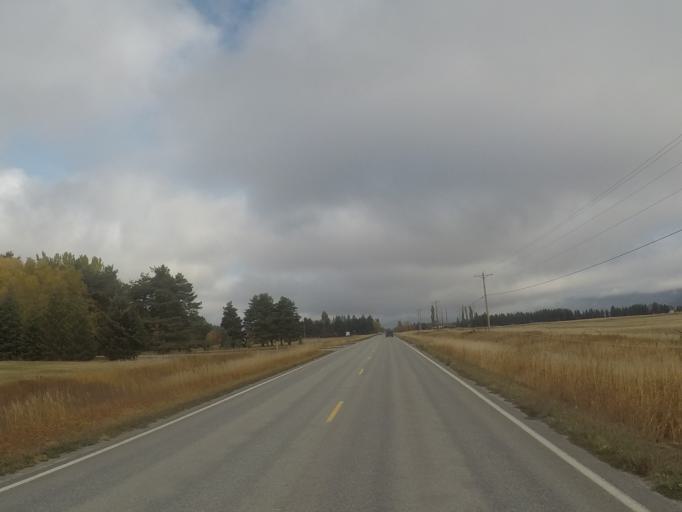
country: US
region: Montana
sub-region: Flathead County
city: Columbia Falls
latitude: 48.3282
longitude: -114.1594
